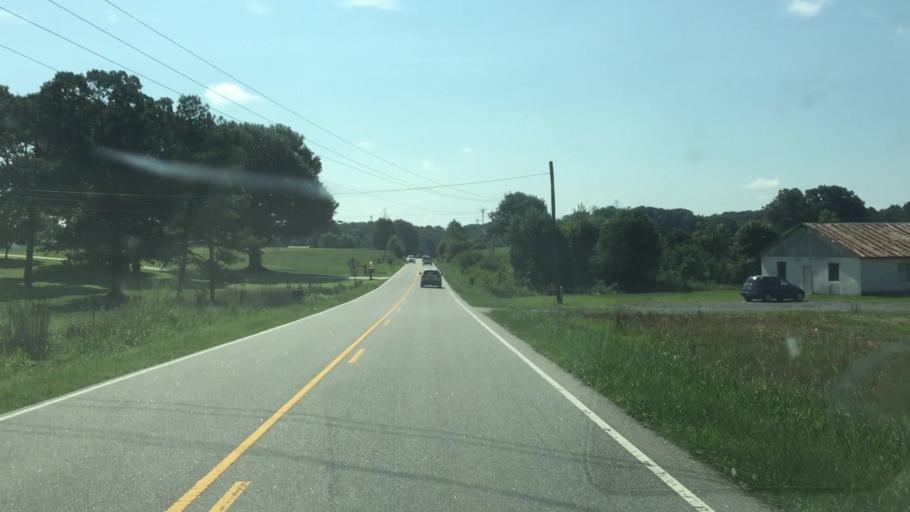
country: US
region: North Carolina
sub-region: Union County
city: Fairview
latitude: 35.1370
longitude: -80.4976
